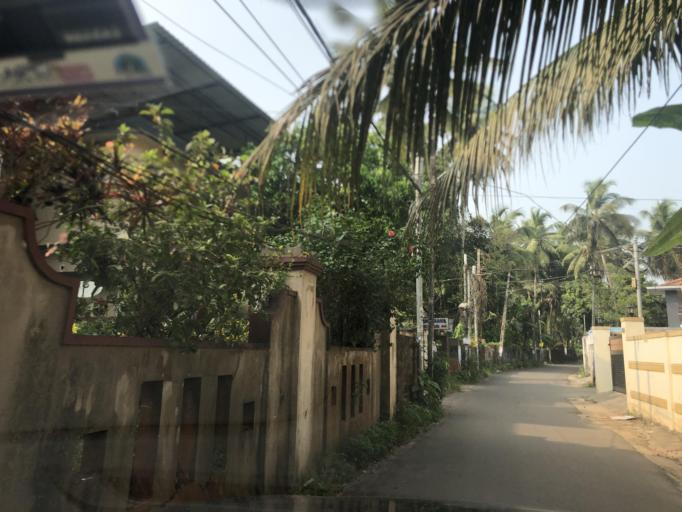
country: IN
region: Kerala
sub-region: Kozhikode
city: Kozhikode
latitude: 11.2825
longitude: 75.7771
